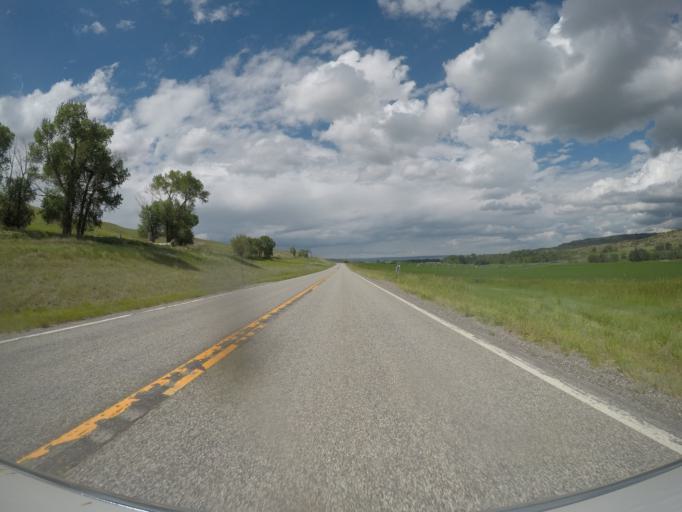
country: US
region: Montana
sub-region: Sweet Grass County
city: Big Timber
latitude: 45.7548
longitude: -109.9924
